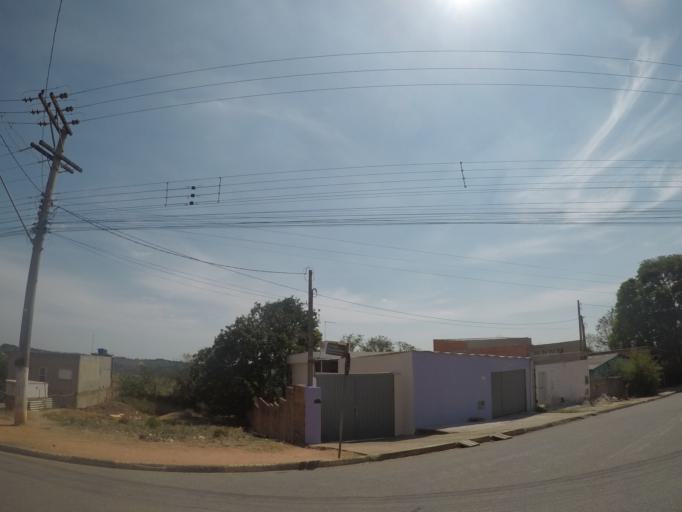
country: BR
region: Sao Paulo
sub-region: Cabreuva
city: Cabreuva
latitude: -23.2761
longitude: -47.0601
